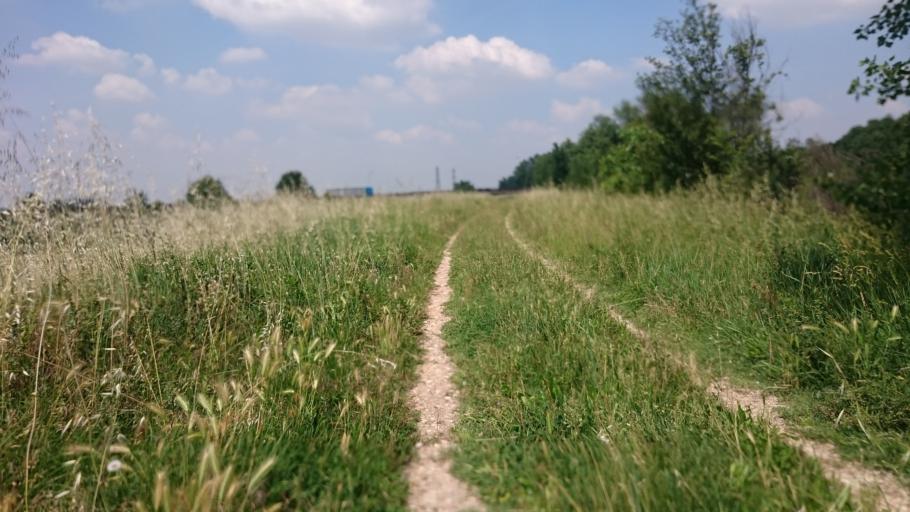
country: IT
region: Lombardy
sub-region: Provincia di Mantova
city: San Biagio
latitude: 45.1101
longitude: 10.8663
